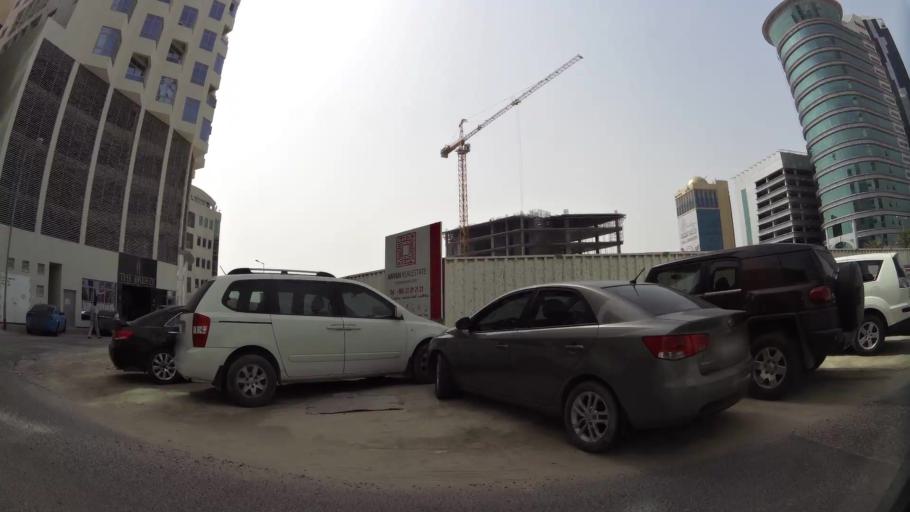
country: BH
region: Manama
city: Jidd Hafs
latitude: 26.2363
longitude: 50.5377
